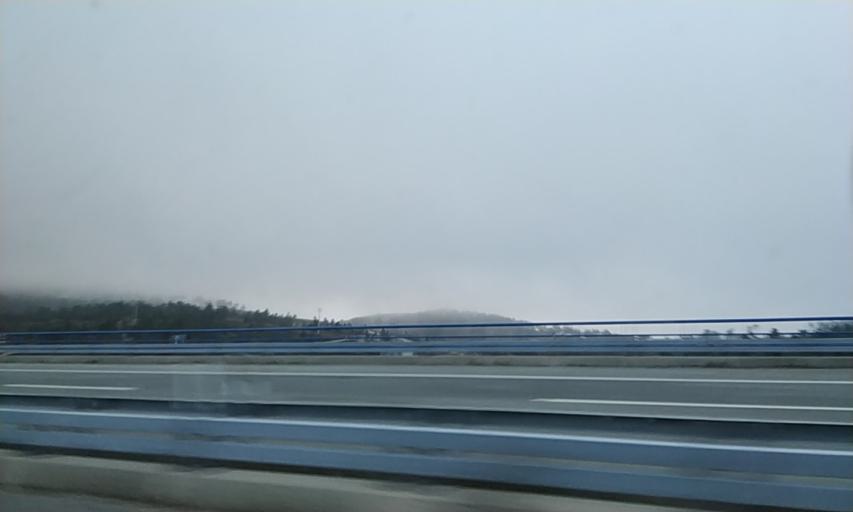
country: PT
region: Vila Real
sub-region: Ribeira de Pena
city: Ribeira de Pena
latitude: 41.5080
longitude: -7.7361
